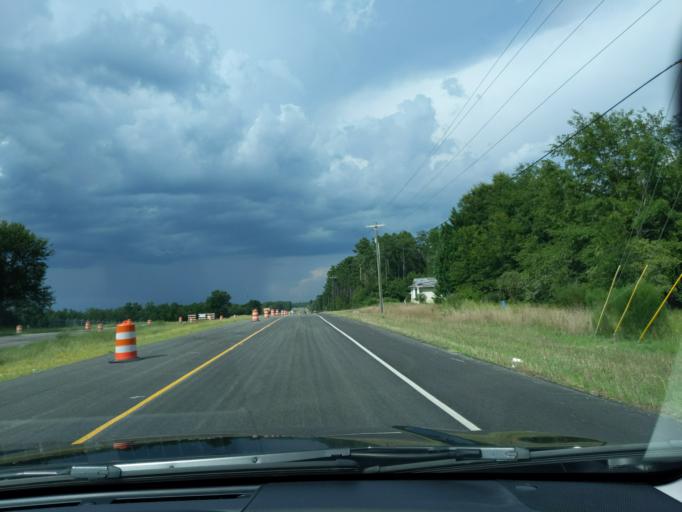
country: US
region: South Carolina
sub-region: Edgefield County
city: Murphys Estates
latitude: 33.6508
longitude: -81.8988
